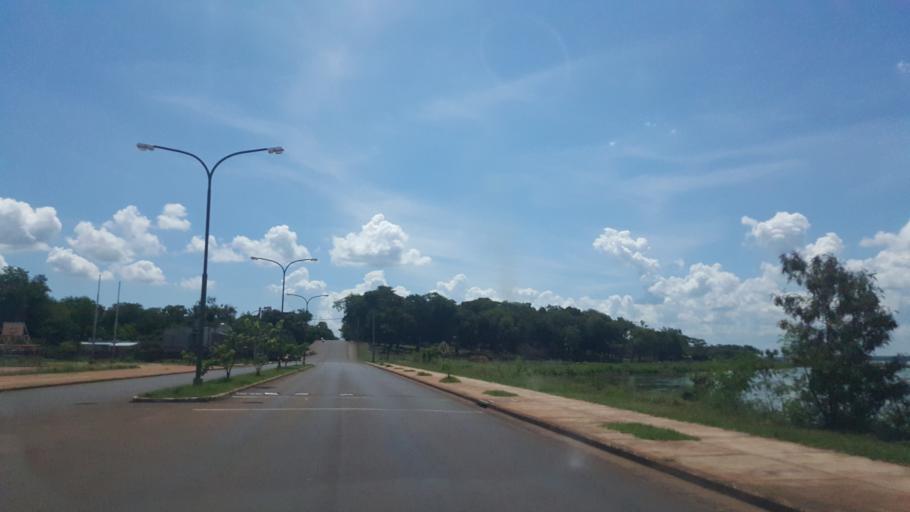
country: AR
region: Misiones
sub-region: Departamento de Capital
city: Posadas
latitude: -27.3627
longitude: -55.9423
